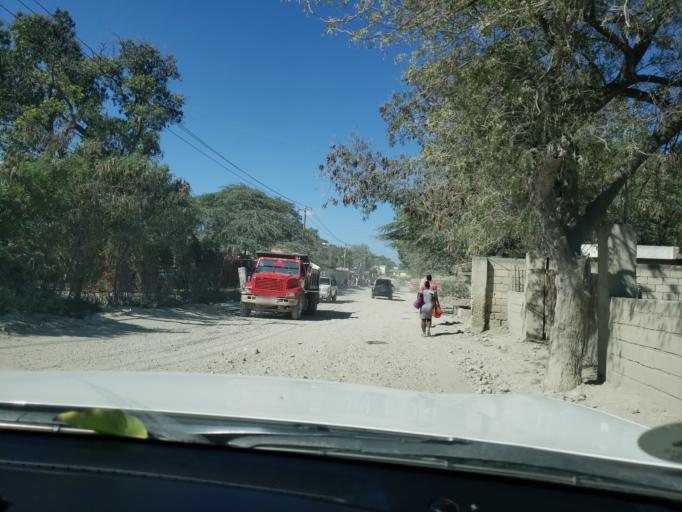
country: HT
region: Ouest
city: Croix des Bouquets
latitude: 18.5733
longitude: -72.2254
